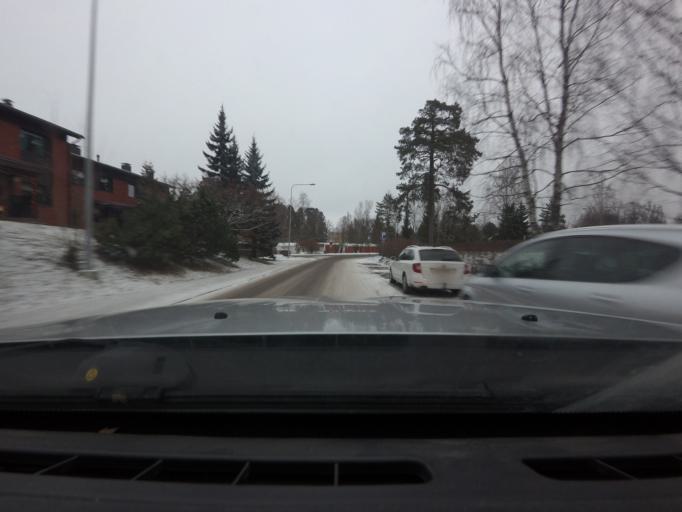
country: FI
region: Uusimaa
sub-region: Helsinki
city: Kauniainen
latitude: 60.2301
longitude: 24.7390
